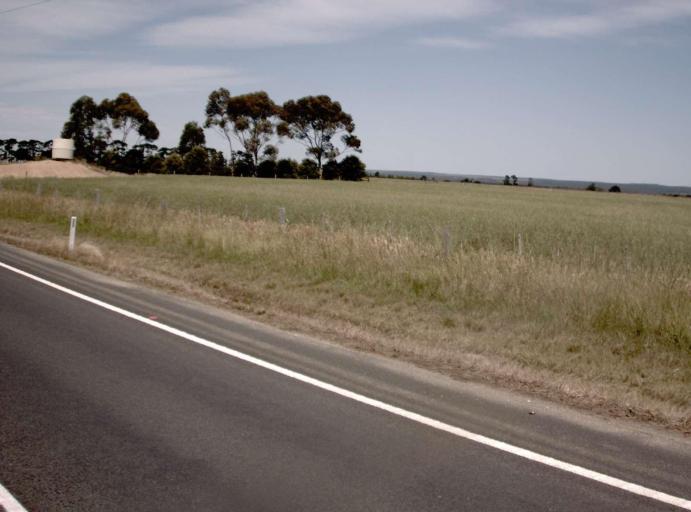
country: AU
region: Victoria
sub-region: Wellington
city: Sale
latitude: -38.1047
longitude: 146.9182
